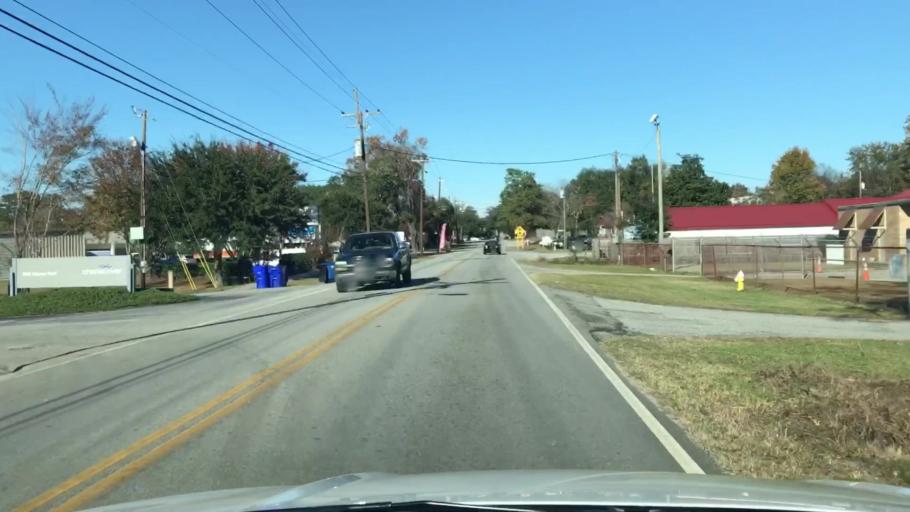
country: US
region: South Carolina
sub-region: Charleston County
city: North Charleston
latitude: 32.7968
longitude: -80.0161
